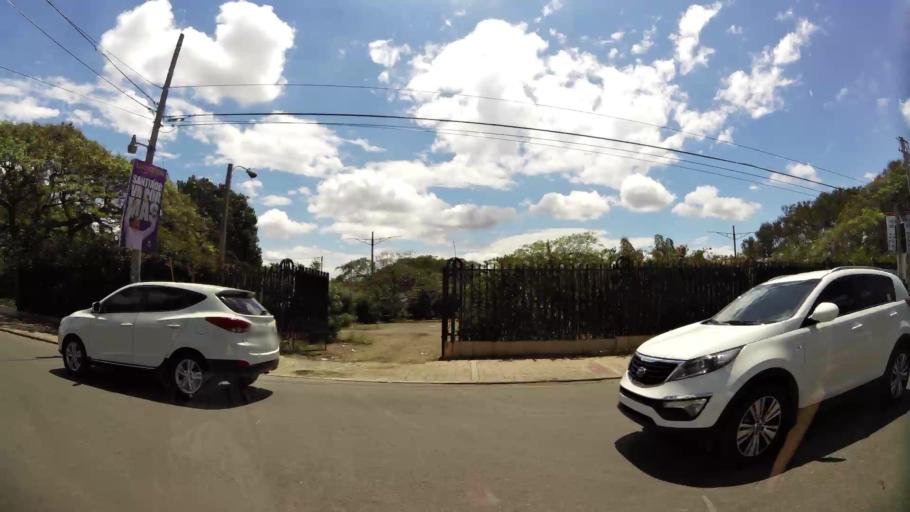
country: DO
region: Santiago
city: Santiago de los Caballeros
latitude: 19.4635
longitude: -70.6733
